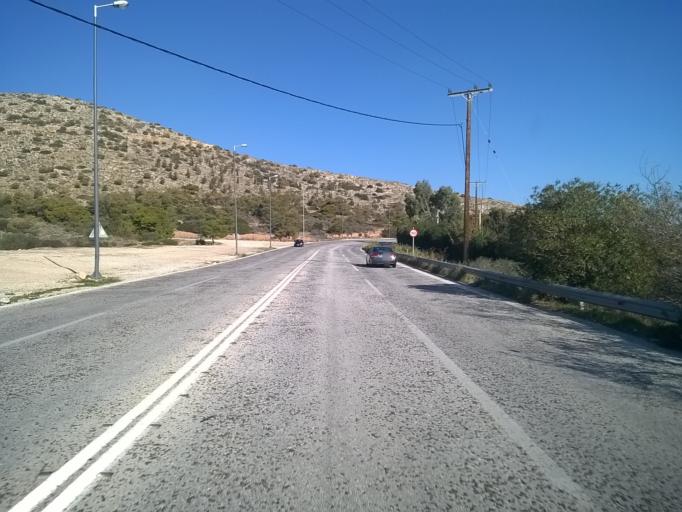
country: GR
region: Attica
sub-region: Nomarchia Anatolikis Attikis
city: Vouliagmeni
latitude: 37.8059
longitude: 23.7985
